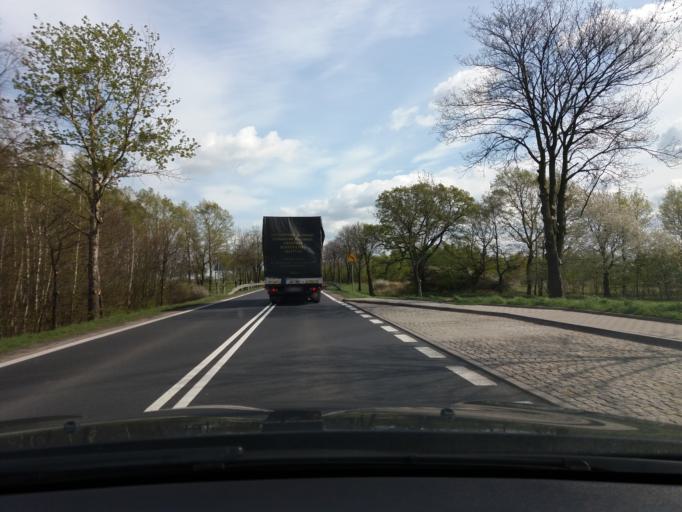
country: PL
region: Lower Silesian Voivodeship
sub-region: Powiat sredzki
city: Ciechow
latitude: 51.1710
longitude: 16.5434
